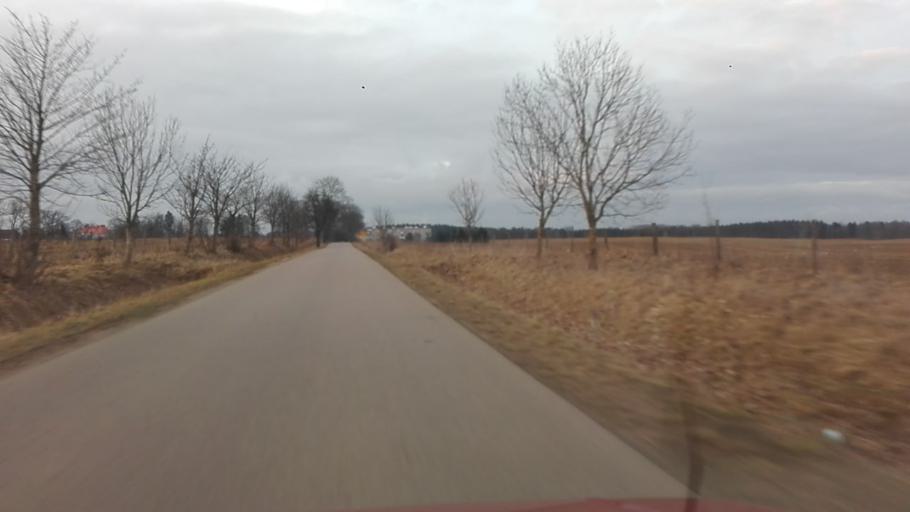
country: PL
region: West Pomeranian Voivodeship
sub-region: Powiat swidwinski
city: Rabino
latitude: 53.8181
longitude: 15.9262
